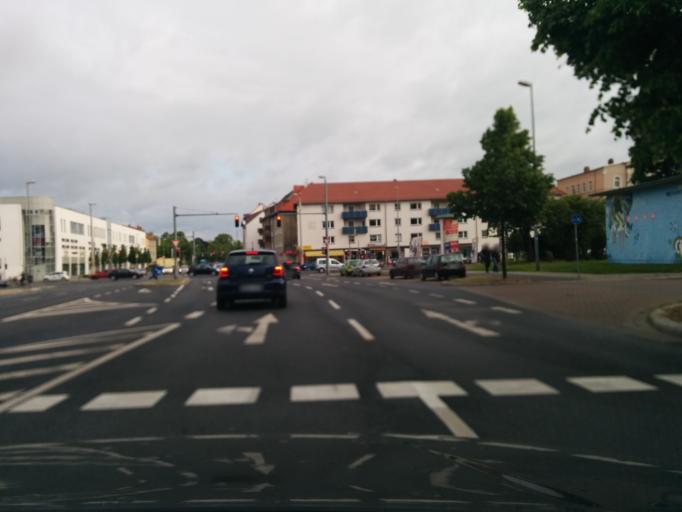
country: DE
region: Lower Saxony
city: Braunschweig
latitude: 52.2718
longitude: 10.5076
